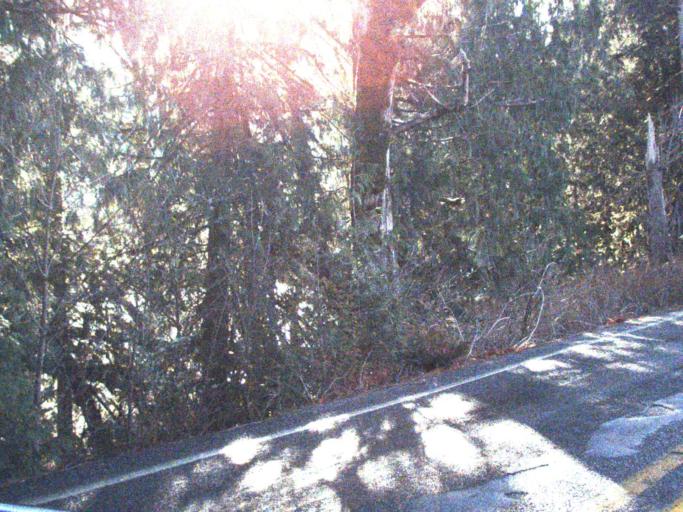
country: US
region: Washington
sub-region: Snohomish County
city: Darrington
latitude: 48.5156
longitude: -121.4660
